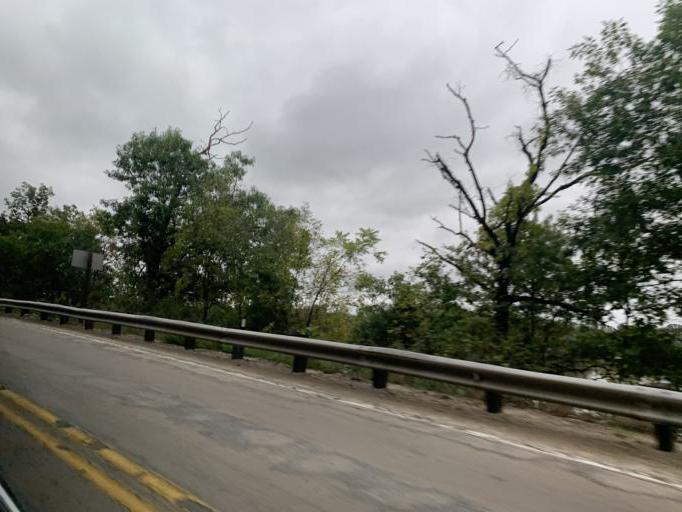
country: US
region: Wisconsin
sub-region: Grant County
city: Muscoda
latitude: 43.2112
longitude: -90.3531
